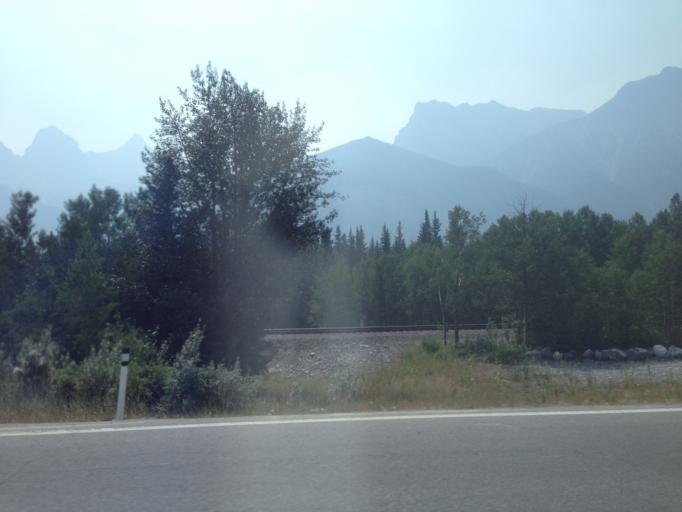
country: CA
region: Alberta
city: Canmore
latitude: 51.0751
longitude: -115.3350
